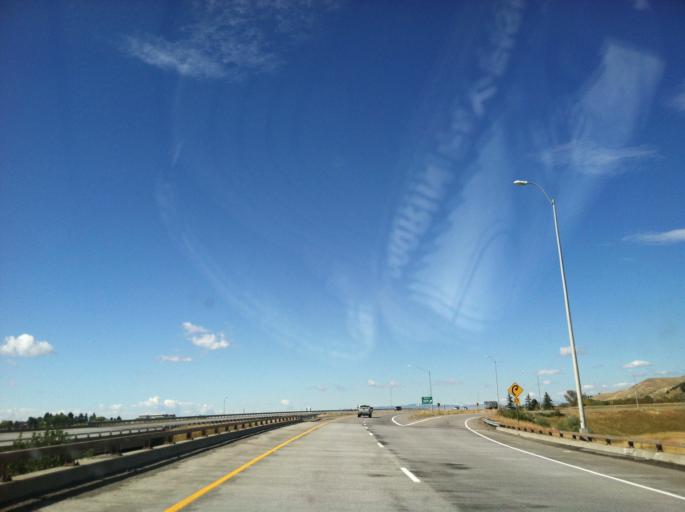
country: US
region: Montana
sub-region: Gallatin County
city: Bozeman
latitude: 45.6752
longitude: -111.0103
